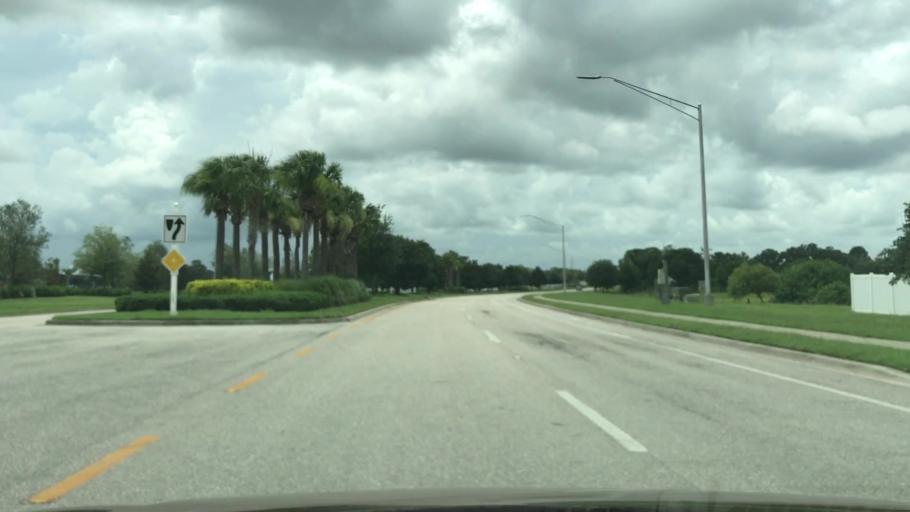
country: US
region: Florida
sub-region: Sarasota County
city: The Meadows
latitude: 27.4392
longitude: -82.4125
